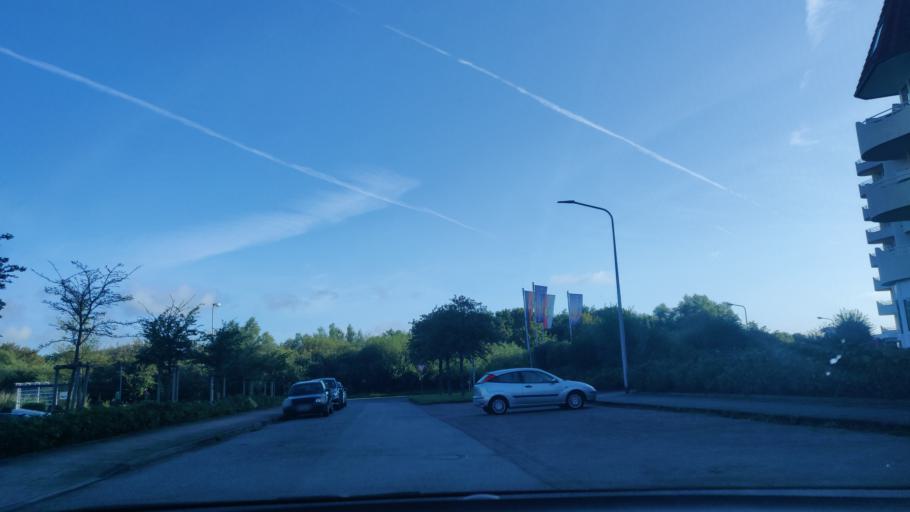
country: DE
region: Lower Saxony
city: Cuxhaven
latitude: 53.8885
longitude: 8.6708
